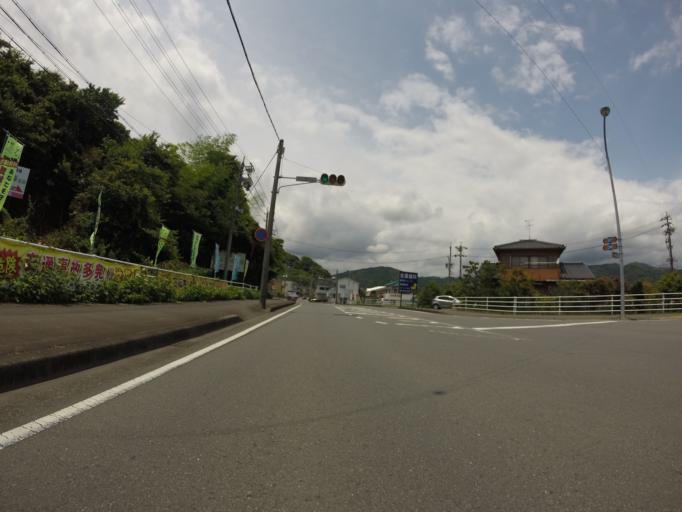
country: JP
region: Shizuoka
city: Shizuoka-shi
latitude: 34.9753
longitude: 138.3405
